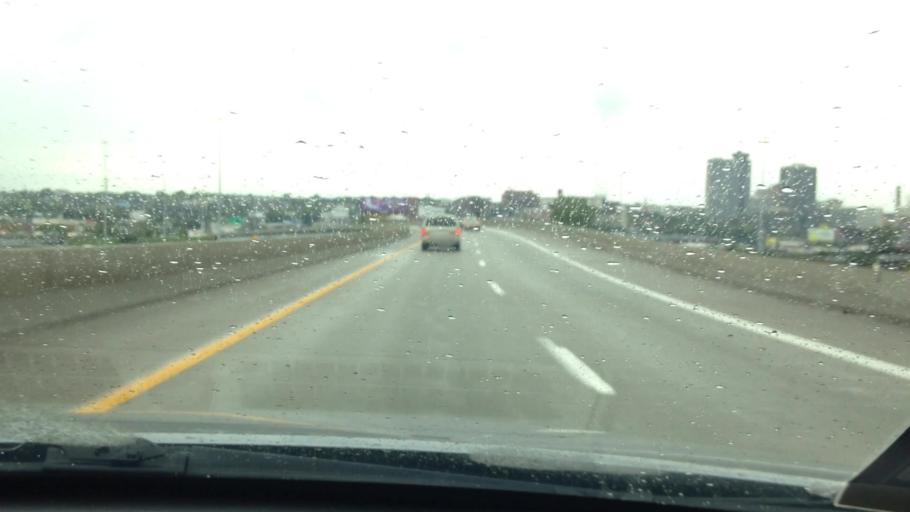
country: US
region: Missouri
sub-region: Jackson County
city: Kansas City
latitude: 39.0987
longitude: -94.5728
